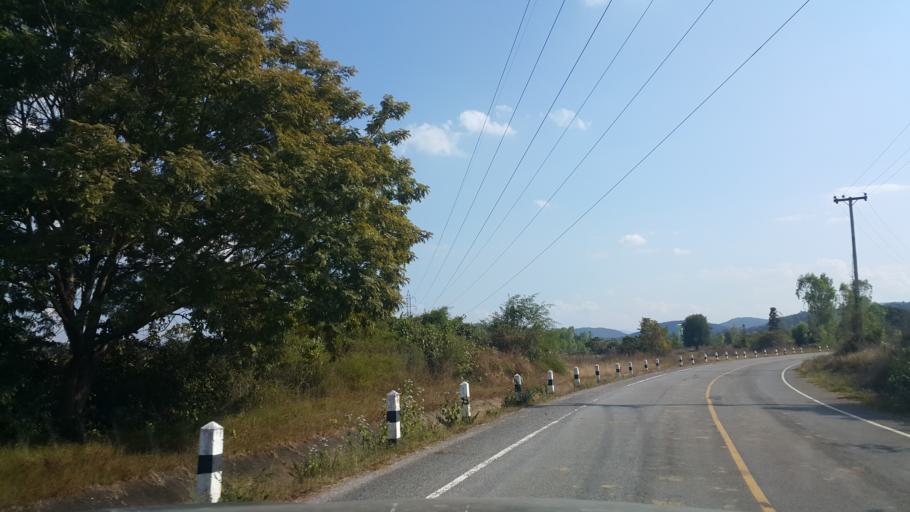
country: TH
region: Lamphun
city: Mae Tha
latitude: 18.5339
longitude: 99.0976
